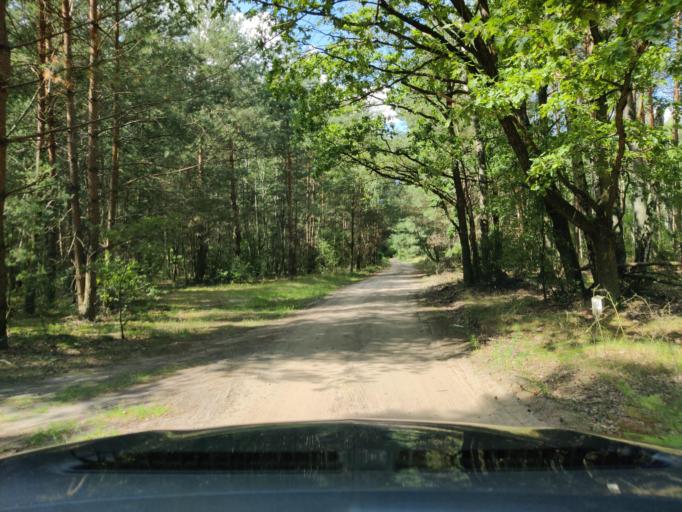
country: PL
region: Masovian Voivodeship
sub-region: Powiat pultuski
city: Pultusk
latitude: 52.7315
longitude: 21.1507
